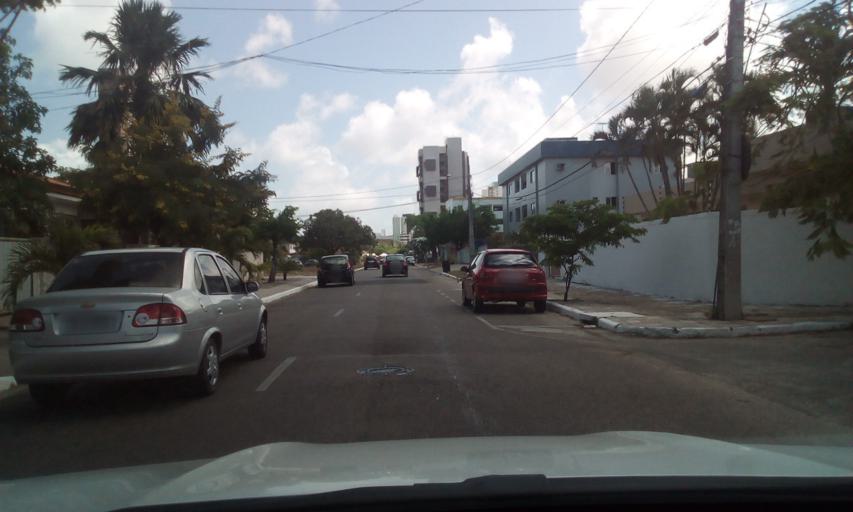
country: BR
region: Paraiba
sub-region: Joao Pessoa
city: Joao Pessoa
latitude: -7.0740
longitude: -34.8382
